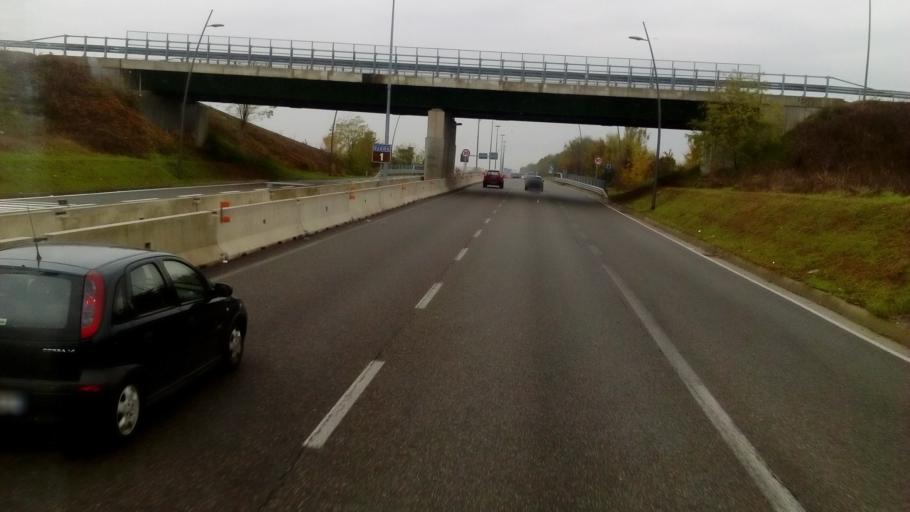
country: IT
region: Lombardy
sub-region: Provincia di Bergamo
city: Treviolo
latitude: 45.6613
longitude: 9.6091
